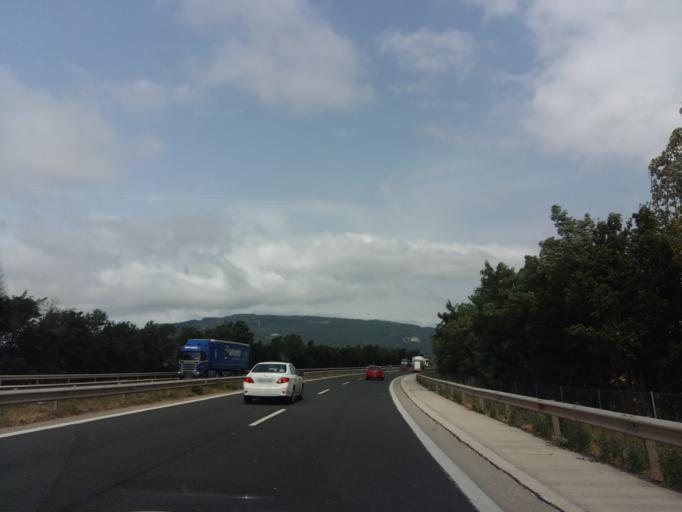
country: ES
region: Navarre
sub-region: Provincia de Navarra
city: Orkoien
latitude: 42.8315
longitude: -1.7075
